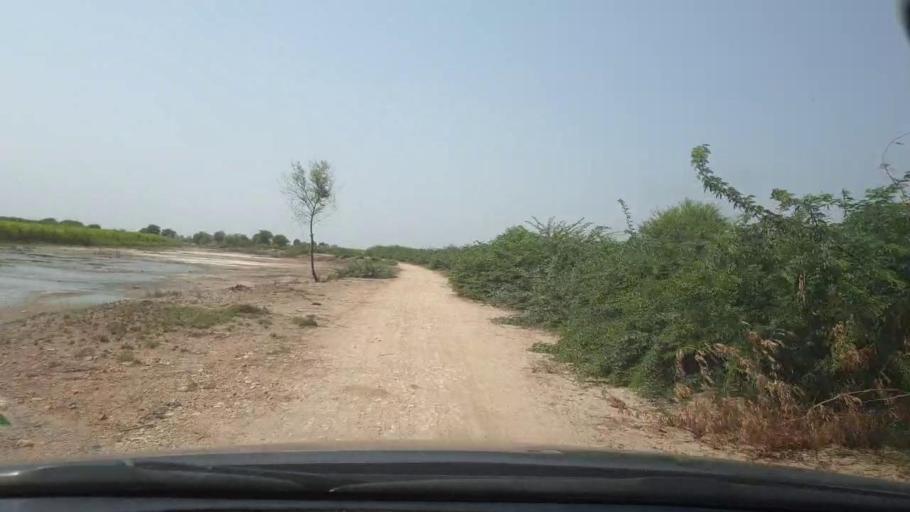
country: PK
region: Sindh
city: Tando Bago
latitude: 24.7735
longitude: 69.1777
